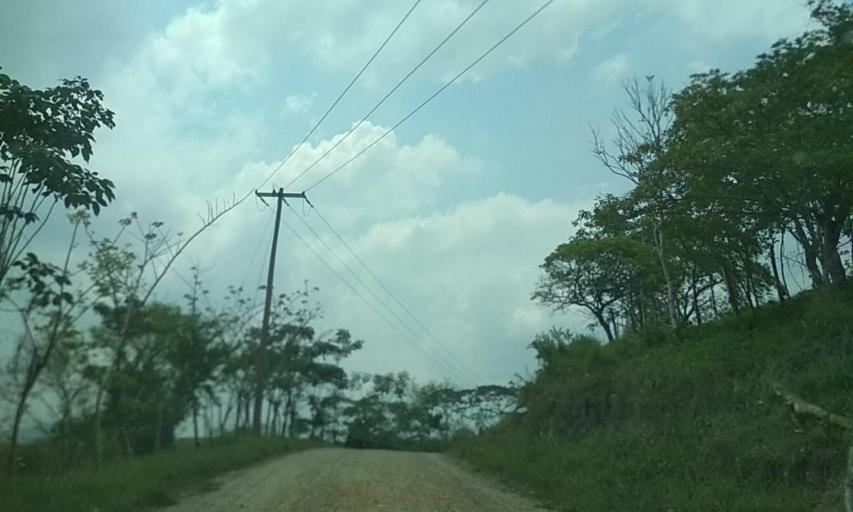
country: MX
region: Tabasco
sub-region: Huimanguillo
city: Francisco Rueda
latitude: 17.6043
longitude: -93.8046
